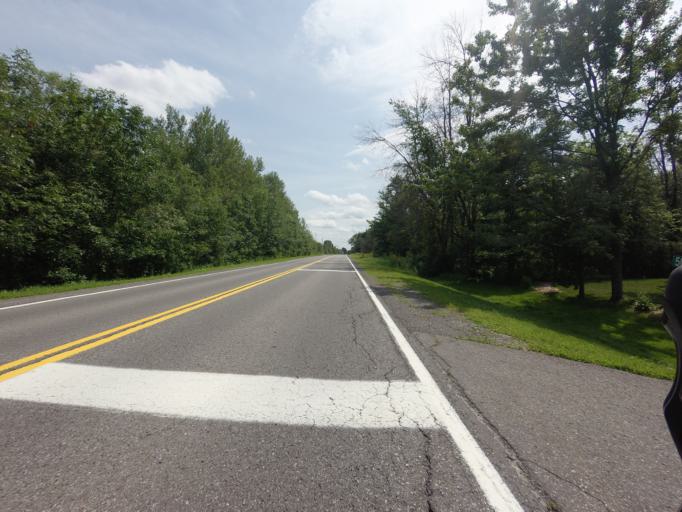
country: CA
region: Ontario
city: Ottawa
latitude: 45.2778
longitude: -75.6269
